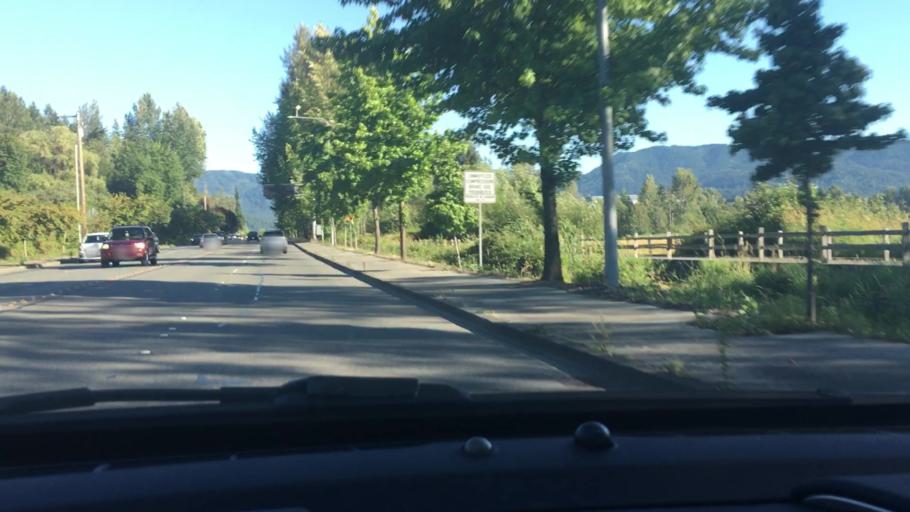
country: US
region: Washington
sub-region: King County
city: Issaquah
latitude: 47.5621
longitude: -122.0502
